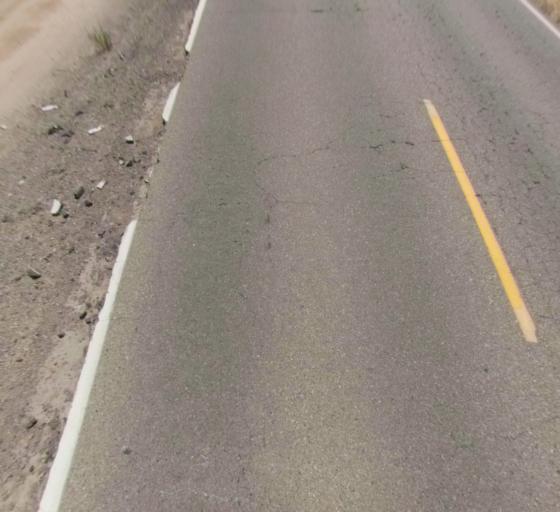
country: US
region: California
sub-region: Madera County
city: Parkwood
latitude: 36.8481
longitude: -120.1039
